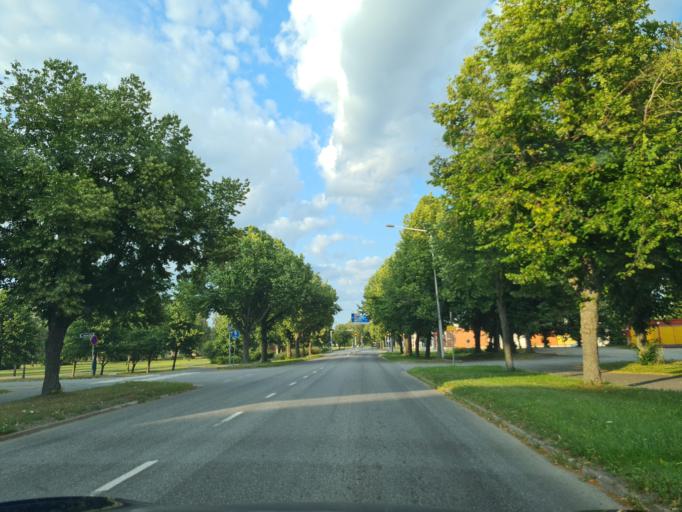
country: FI
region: Southern Ostrobothnia
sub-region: Seinaejoki
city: Lapua
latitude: 62.9727
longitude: 23.0051
